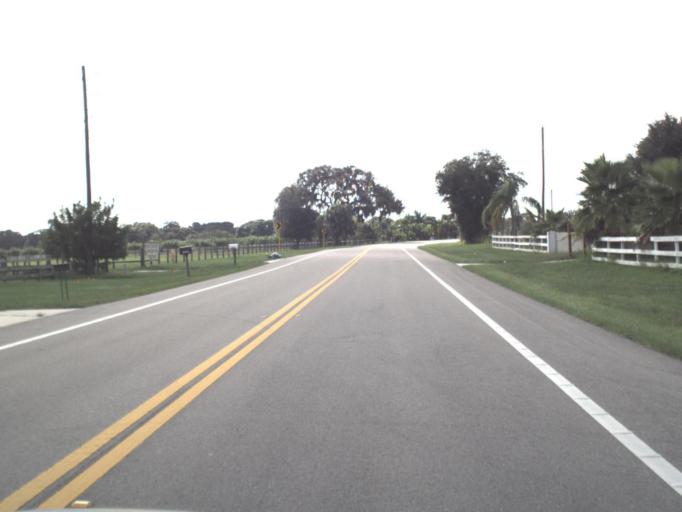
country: US
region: Florida
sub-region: Sarasota County
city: The Meadows
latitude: 27.4742
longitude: -82.2729
